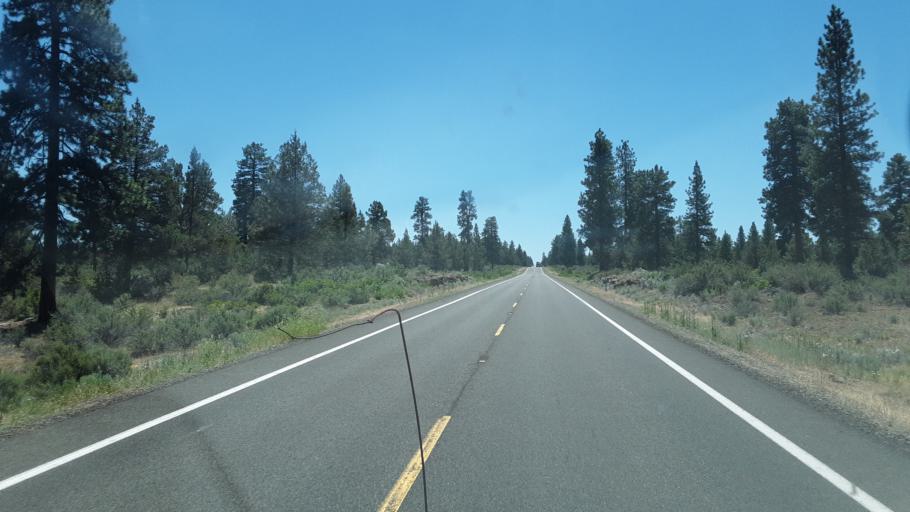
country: US
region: California
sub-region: Siskiyou County
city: Tulelake
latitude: 41.6229
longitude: -121.2212
